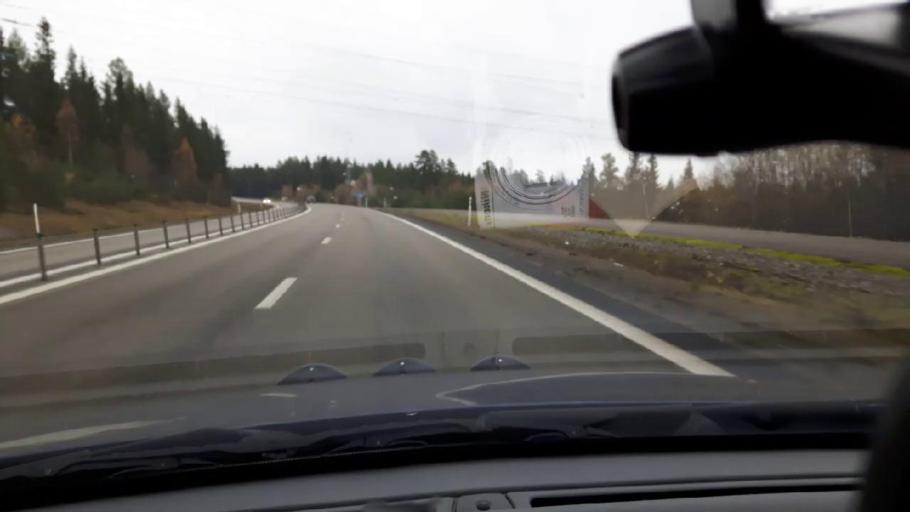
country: SE
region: Jaemtland
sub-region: OEstersunds Kommun
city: Ostersund
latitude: 63.1719
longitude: 14.7025
